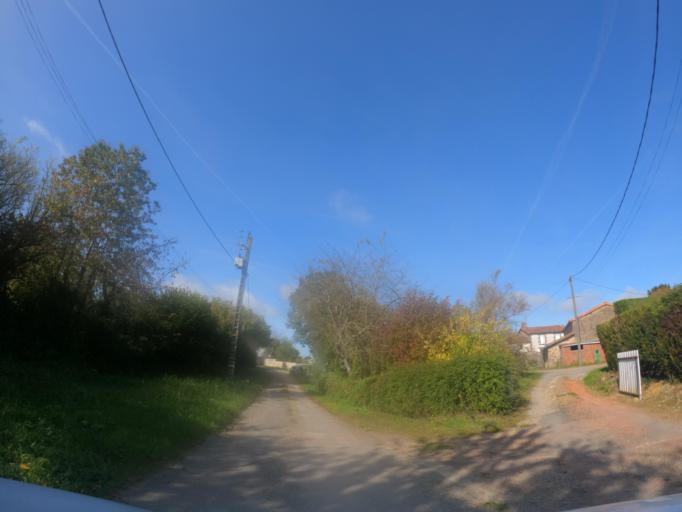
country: FR
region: Poitou-Charentes
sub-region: Departement des Deux-Sevres
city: Courlay
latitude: 46.7934
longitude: -0.5609
